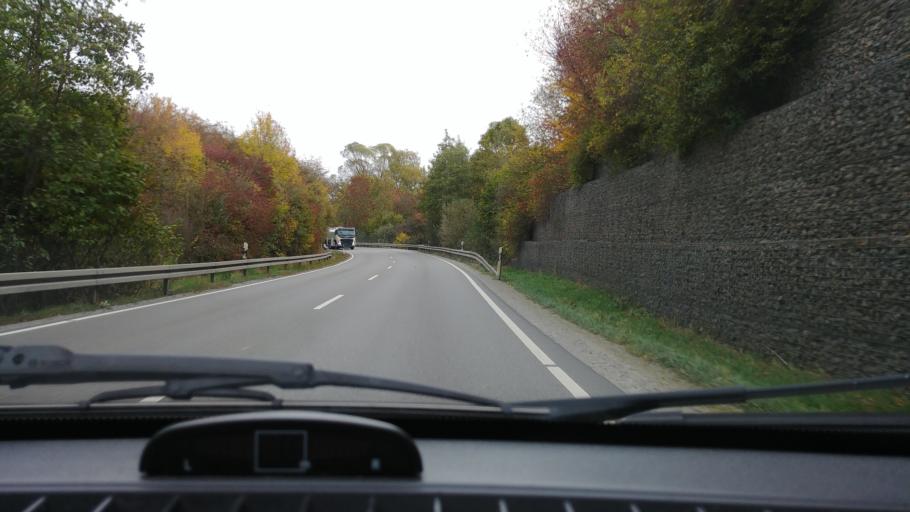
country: DE
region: Baden-Wuerttemberg
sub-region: Regierungsbezirk Stuttgart
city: Crailsheim
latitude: 49.1519
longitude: 10.0715
